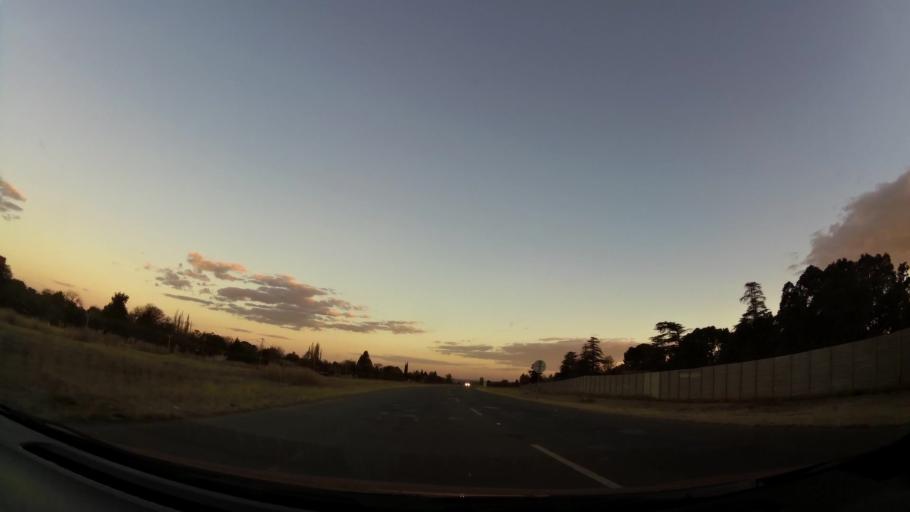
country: ZA
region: North-West
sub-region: Dr Kenneth Kaunda District Municipality
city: Potchefstroom
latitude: -26.6798
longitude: 27.0750
